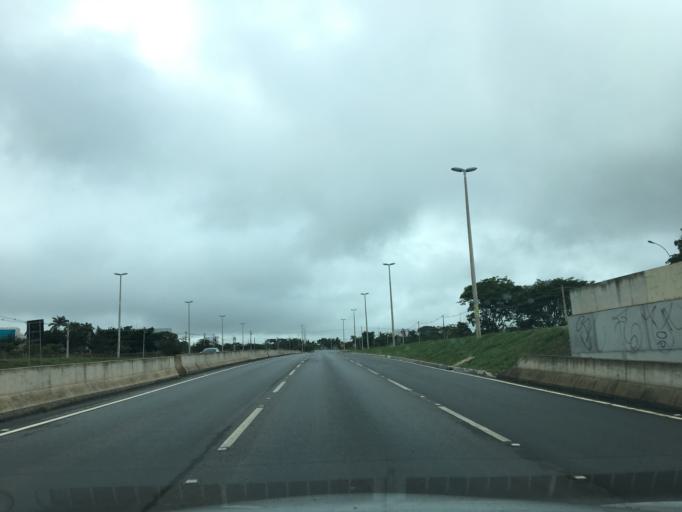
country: BR
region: Federal District
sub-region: Brasilia
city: Brasilia
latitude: -15.8642
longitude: -47.9359
